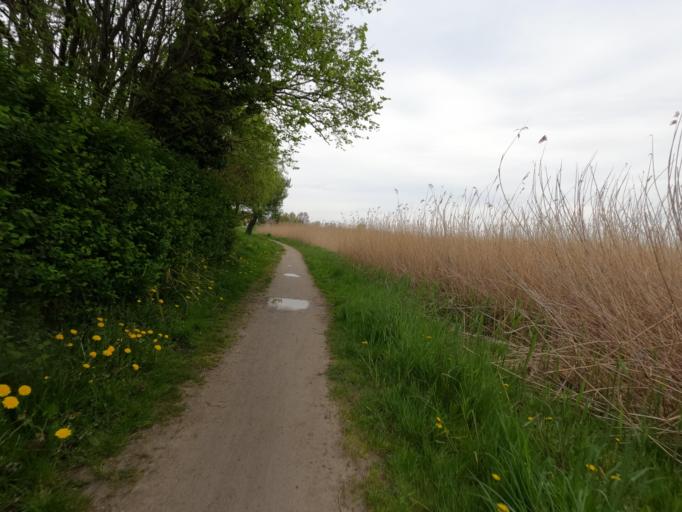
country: DE
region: Mecklenburg-Vorpommern
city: Ostseebad Dierhagen
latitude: 54.3633
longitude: 12.4132
